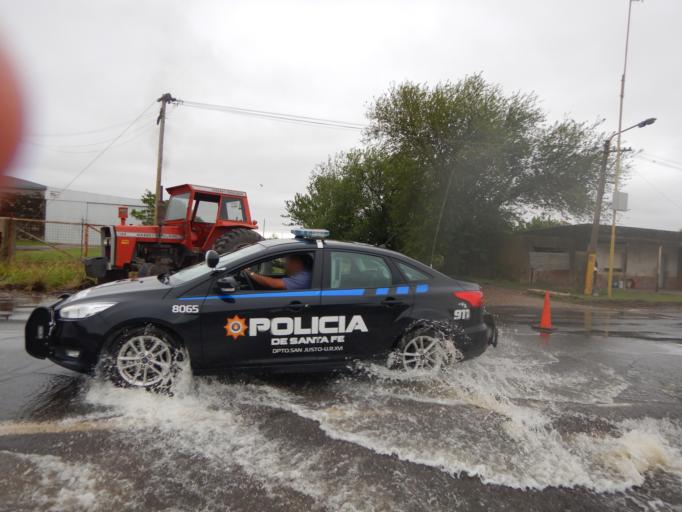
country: AR
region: Santa Fe
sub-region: Departamento de San Justo
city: San Justo
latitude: -30.9489
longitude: -60.6606
